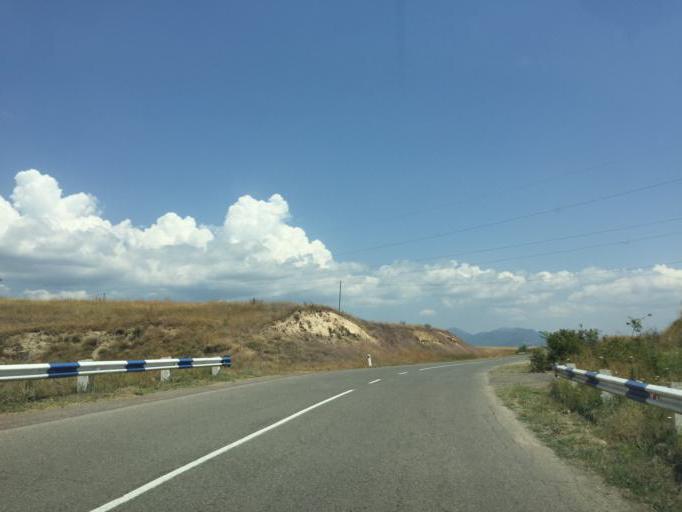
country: AM
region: Syunik'i Marz
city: Tegh
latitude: 39.5848
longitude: 46.4986
